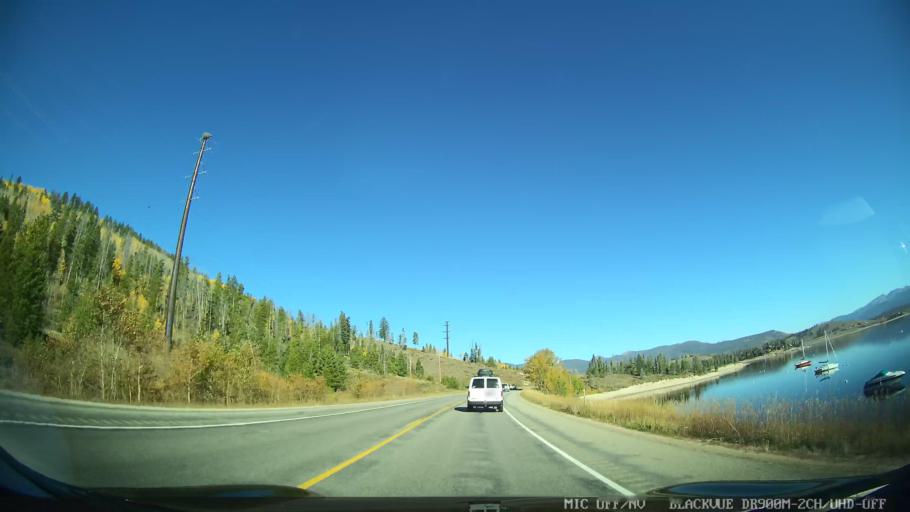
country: US
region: Colorado
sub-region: Grand County
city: Granby
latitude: 40.1618
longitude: -105.8964
